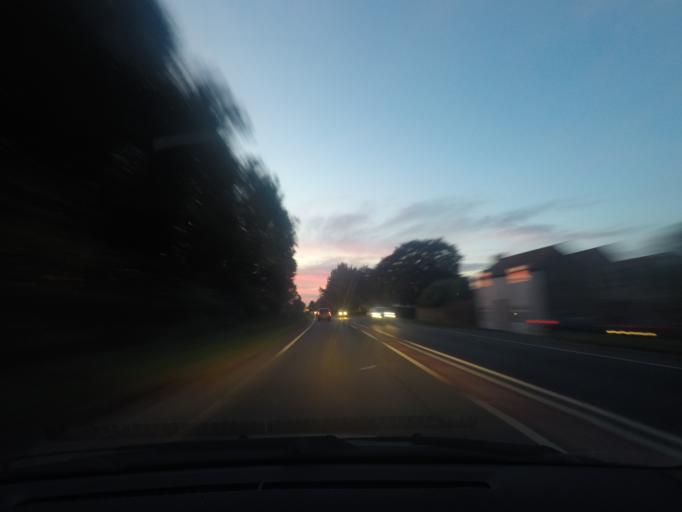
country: GB
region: England
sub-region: East Riding of Yorkshire
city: Pocklington
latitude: 53.9292
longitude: -0.8211
